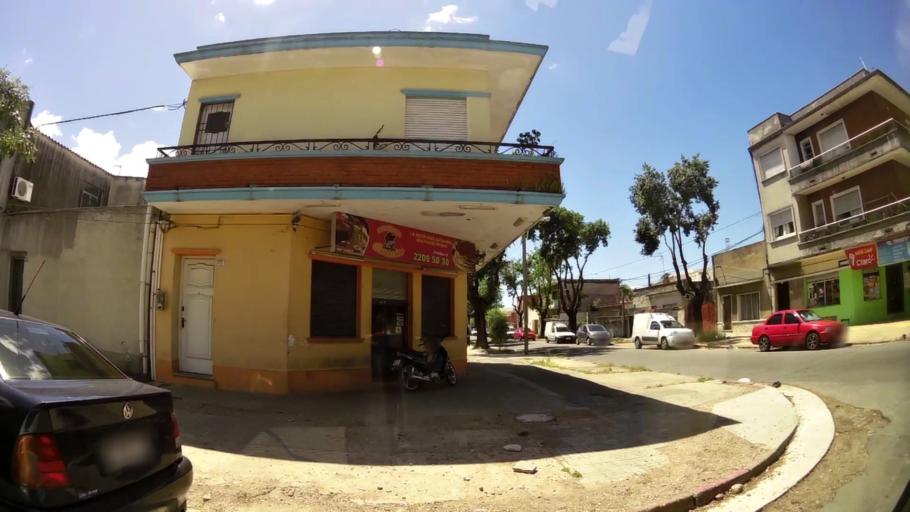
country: UY
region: Montevideo
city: Montevideo
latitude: -34.8750
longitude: -56.1723
